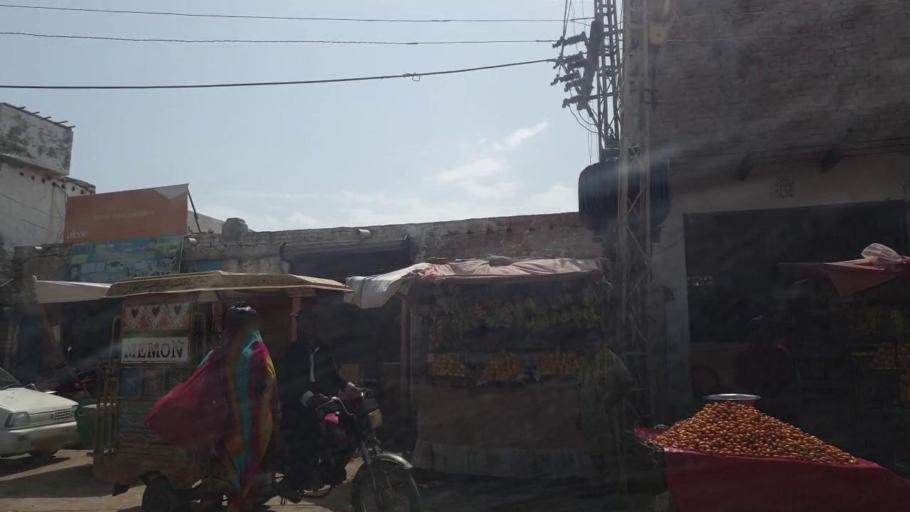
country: PK
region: Sindh
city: Naukot
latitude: 24.7616
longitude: 69.1979
